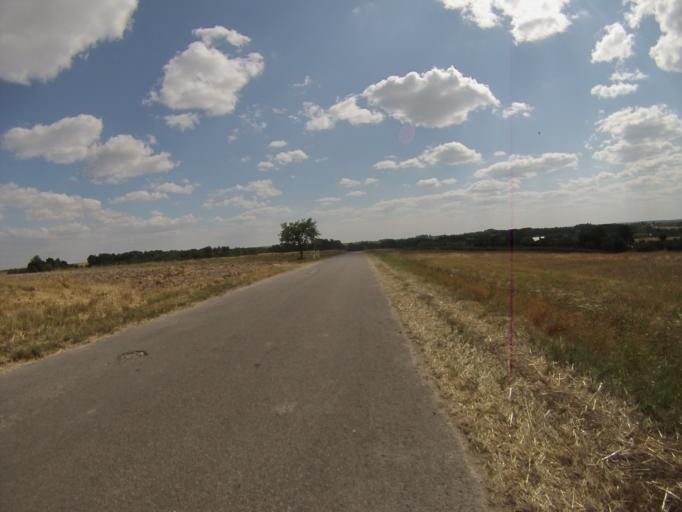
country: PL
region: Swietokrzyskie
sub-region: Powiat kielecki
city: Rakow
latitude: 50.7206
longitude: 21.0724
